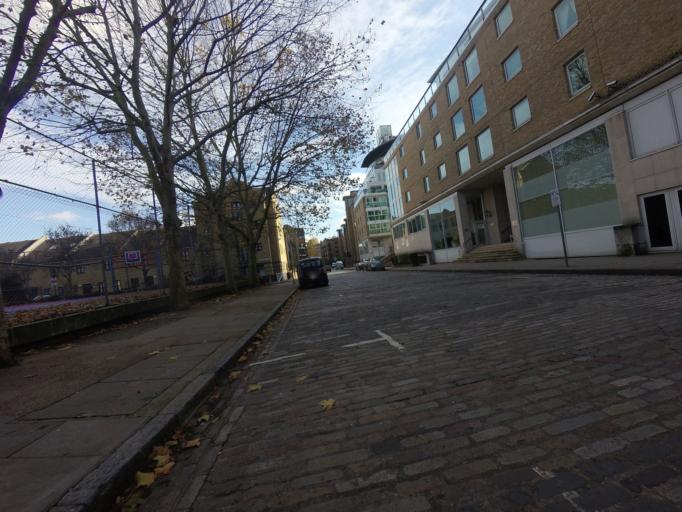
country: GB
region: England
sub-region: Greater London
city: Bethnal Green
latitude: 51.5044
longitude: -0.0658
